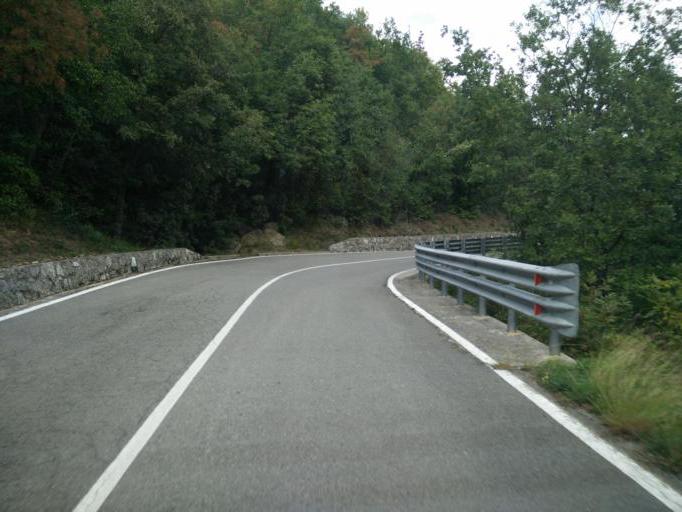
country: IT
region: Tuscany
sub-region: Provincia di Massa-Carrara
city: Casola in Lunigiana
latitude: 44.2070
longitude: 10.2058
